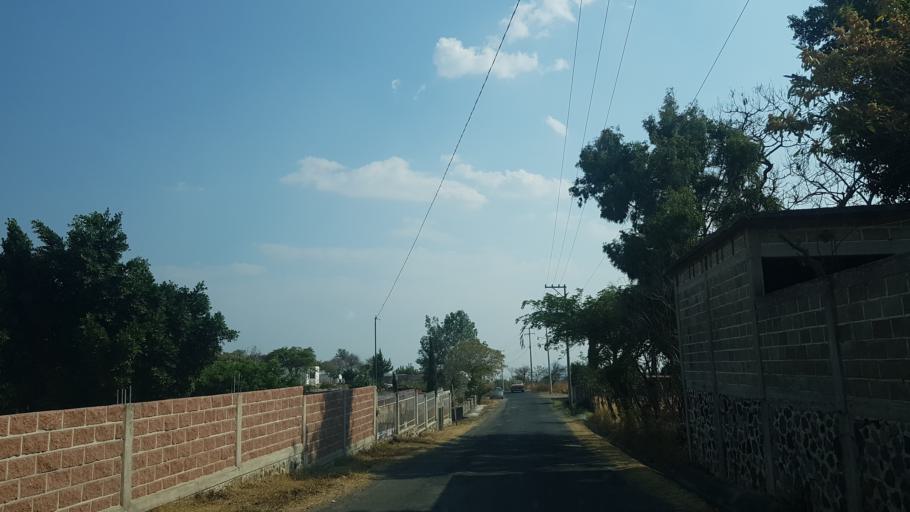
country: MX
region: Morelos
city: Tlacotepec
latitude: 18.8082
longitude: -98.7132
